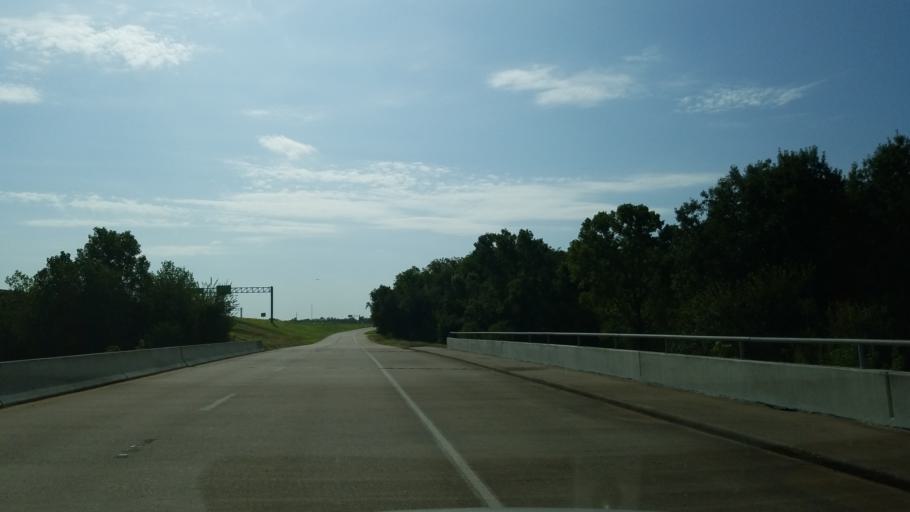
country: US
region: Texas
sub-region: Tarrant County
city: Grapevine
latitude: 32.8956
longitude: -97.0876
